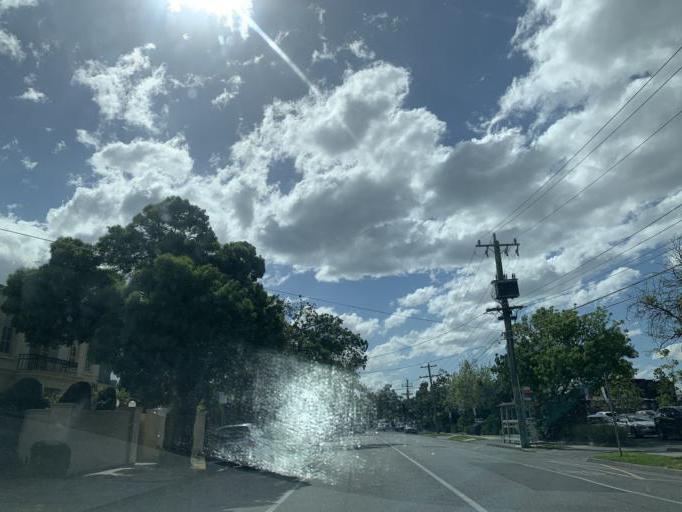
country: AU
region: Victoria
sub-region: Bayside
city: North Brighton
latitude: -37.9159
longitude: 144.9947
